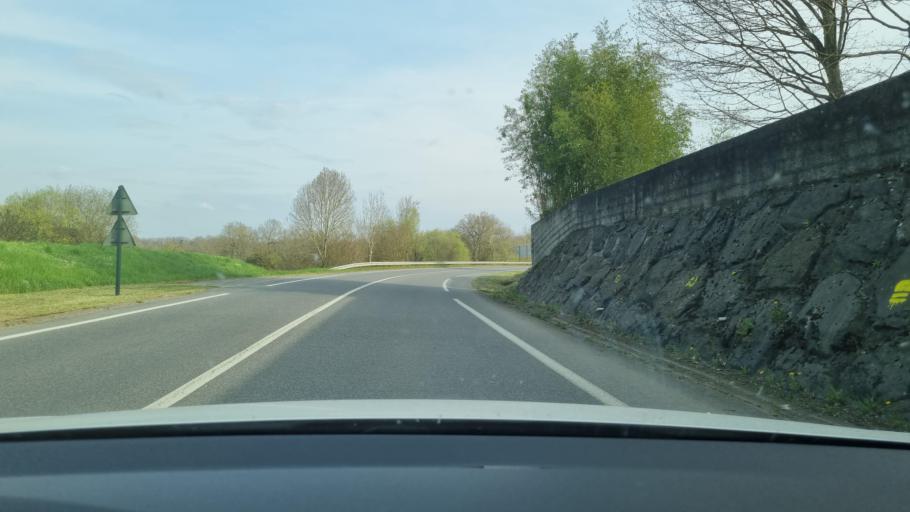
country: FR
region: Aquitaine
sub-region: Departement des Pyrenees-Atlantiques
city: Morlaas
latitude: 43.3501
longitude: -0.2564
